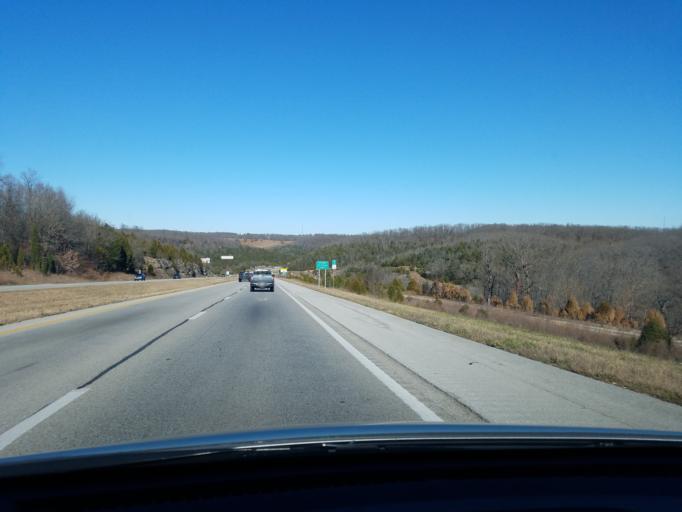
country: US
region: Missouri
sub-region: Taney County
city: Merriam Woods
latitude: 36.8146
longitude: -93.2257
